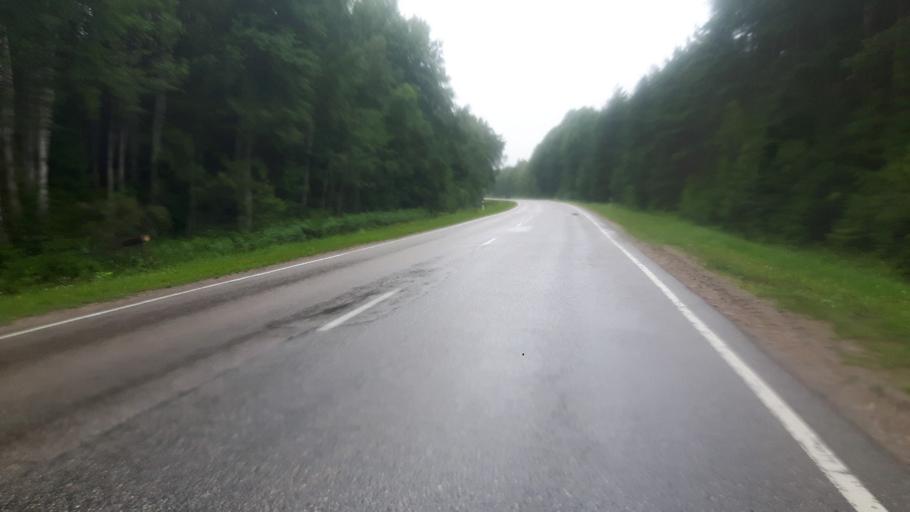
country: LV
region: Rucavas
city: Rucava
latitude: 56.1385
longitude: 21.1523
